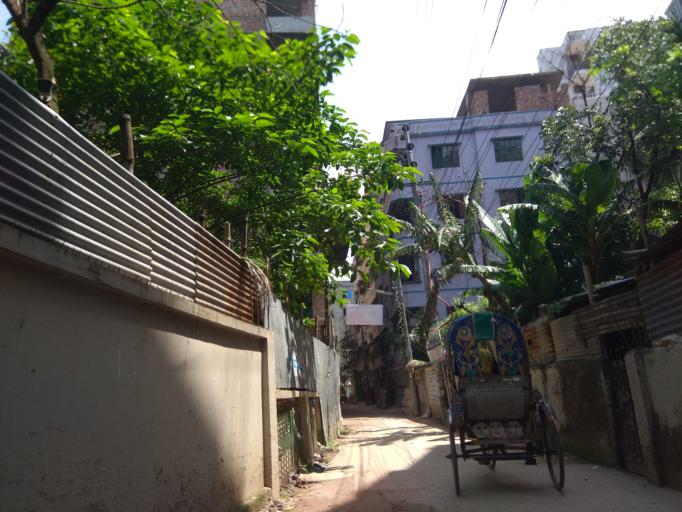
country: BD
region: Dhaka
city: Tungi
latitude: 23.8186
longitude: 90.3933
